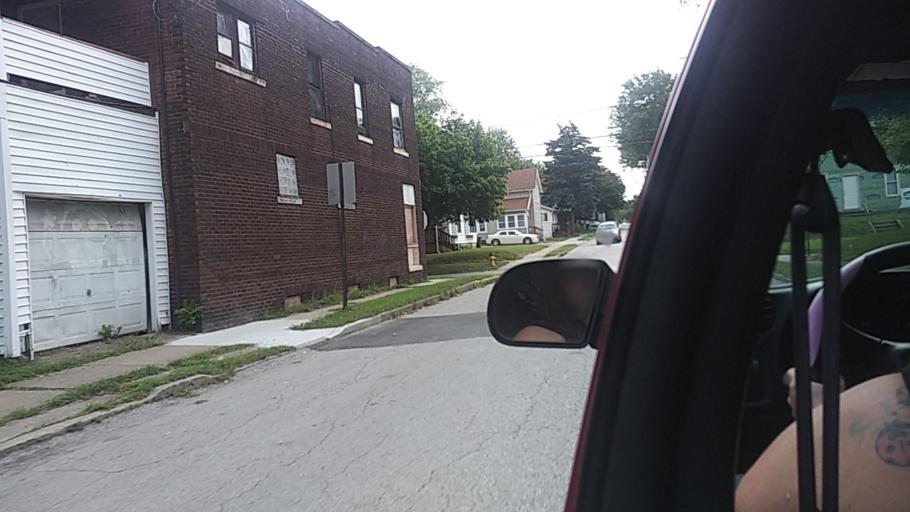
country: US
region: Ohio
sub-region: Summit County
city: Akron
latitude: 41.0638
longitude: -81.5138
